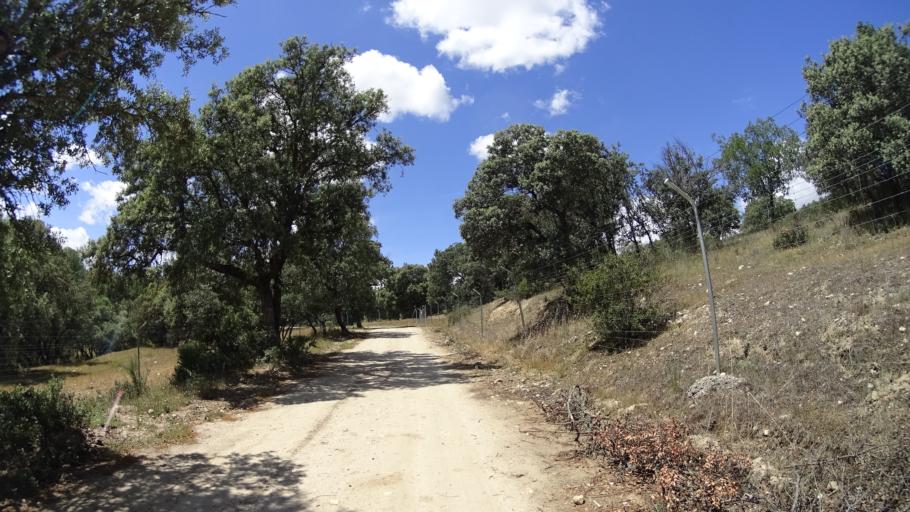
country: ES
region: Madrid
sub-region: Provincia de Madrid
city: Villanueva de la Canada
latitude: 40.4367
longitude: -3.9597
